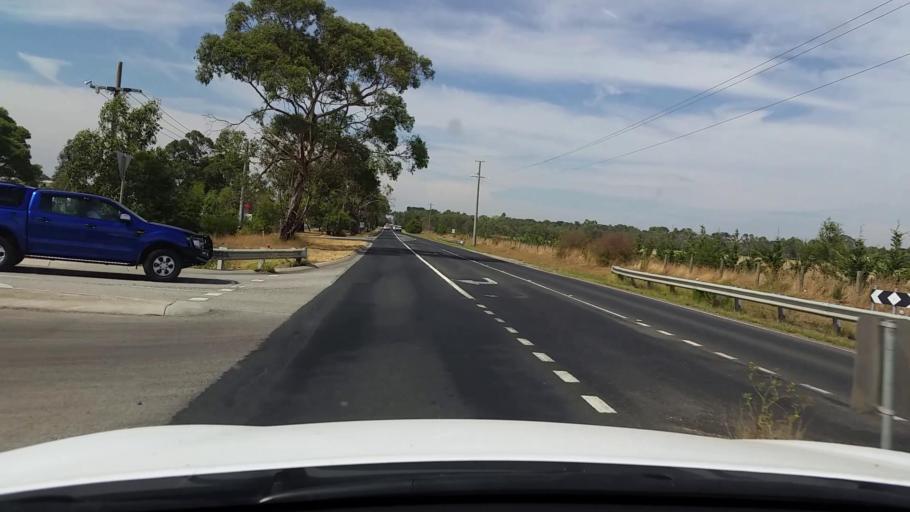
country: AU
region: Victoria
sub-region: Mornington Peninsula
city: Hastings
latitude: -38.2858
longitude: 145.1836
